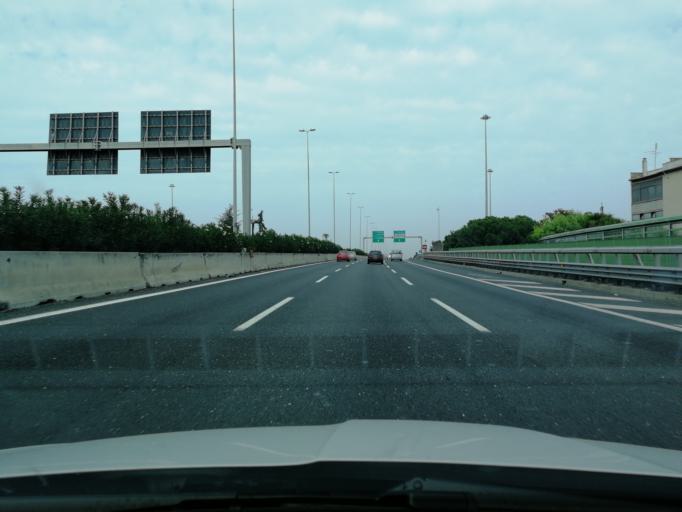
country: IT
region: Latium
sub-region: Citta metropolitana di Roma Capitale
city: Ciampino
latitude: 41.8630
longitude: 12.6004
